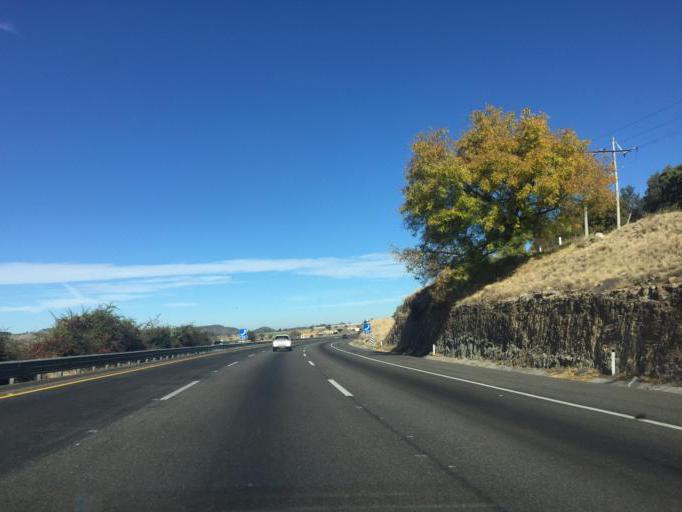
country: MX
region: Mexico
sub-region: Aculco
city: El Colorado
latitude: 20.1204
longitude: -99.7217
